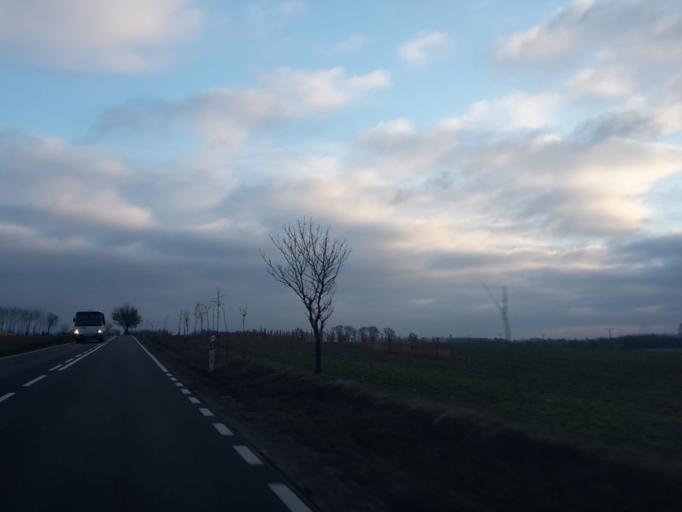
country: PL
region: Warmian-Masurian Voivodeship
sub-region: Powiat ilawski
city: Lubawa
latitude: 53.5894
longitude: 19.8467
